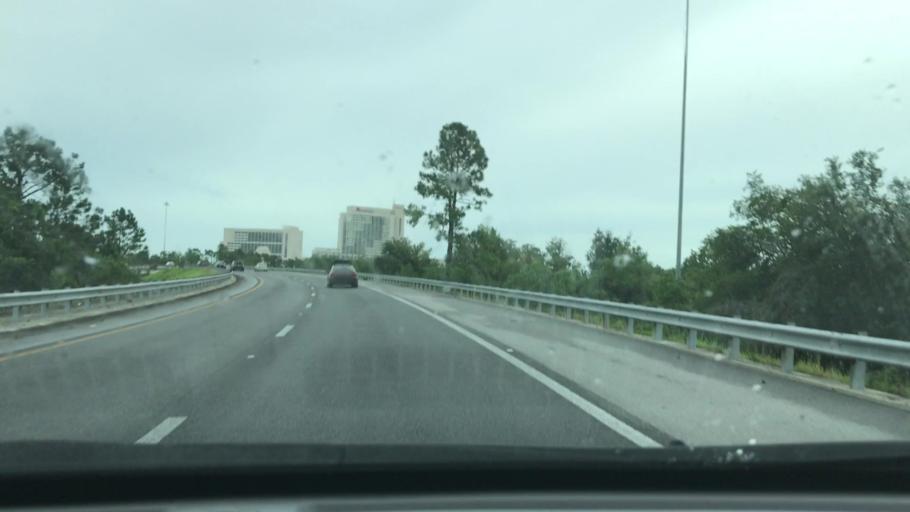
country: US
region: Florida
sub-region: Osceola County
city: Celebration
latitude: 28.3572
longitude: -81.5187
